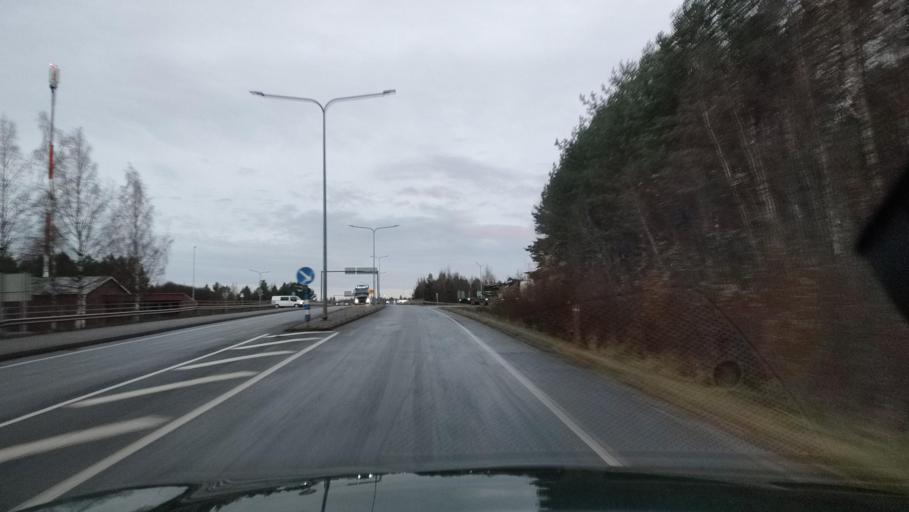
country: FI
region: Ostrobothnia
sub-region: Vaasa
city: Ristinummi
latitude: 63.0302
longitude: 21.7569
